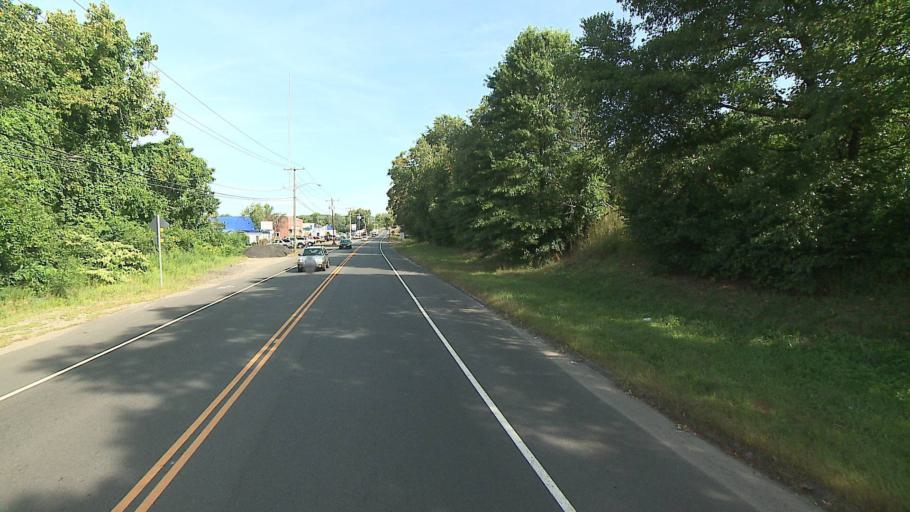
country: US
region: Connecticut
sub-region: New Haven County
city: Waterbury
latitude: 41.5630
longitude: -73.0541
